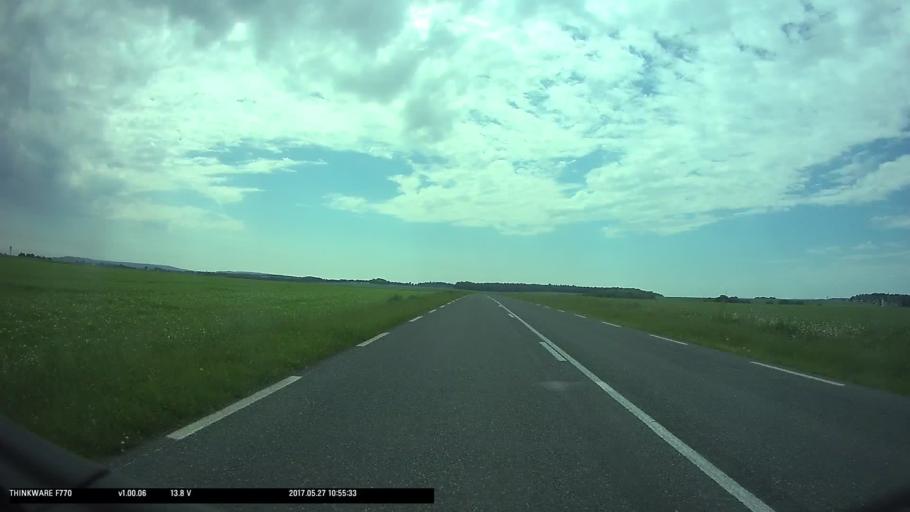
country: FR
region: Picardie
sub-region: Departement de l'Oise
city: Chaumont-en-Vexin
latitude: 49.2308
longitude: 1.8814
